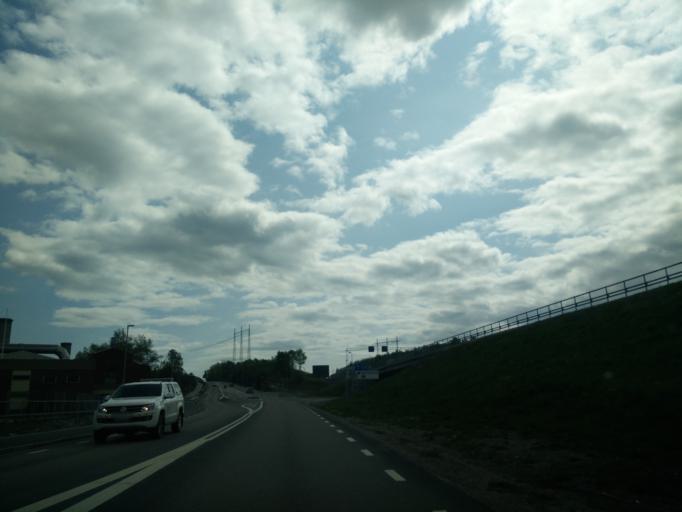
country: SE
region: Vaesternorrland
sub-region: Sundsvalls Kommun
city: Stockvik
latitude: 62.3764
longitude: 17.3626
